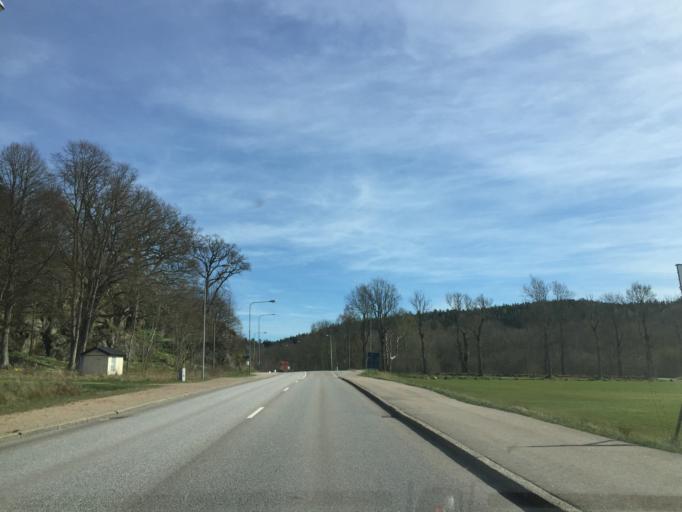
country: SE
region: Vaestra Goetaland
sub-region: Uddevalla Kommun
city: Uddevalla
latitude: 58.3312
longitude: 11.9159
